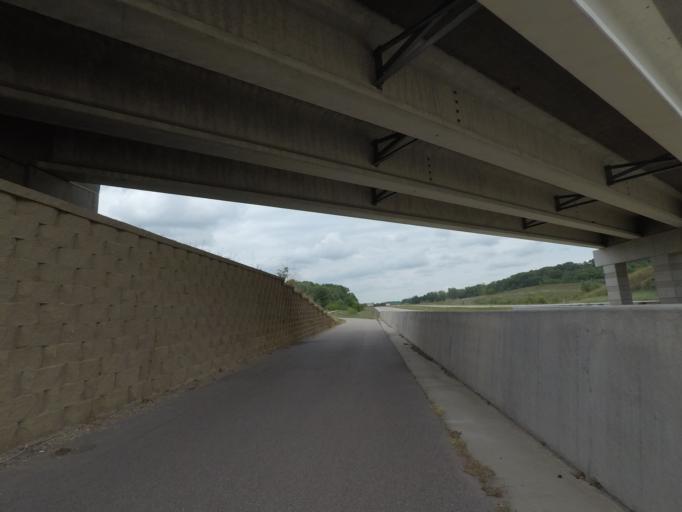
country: US
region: Wisconsin
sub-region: Jefferson County
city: Lake Koshkonong
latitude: 42.8825
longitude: -88.8780
